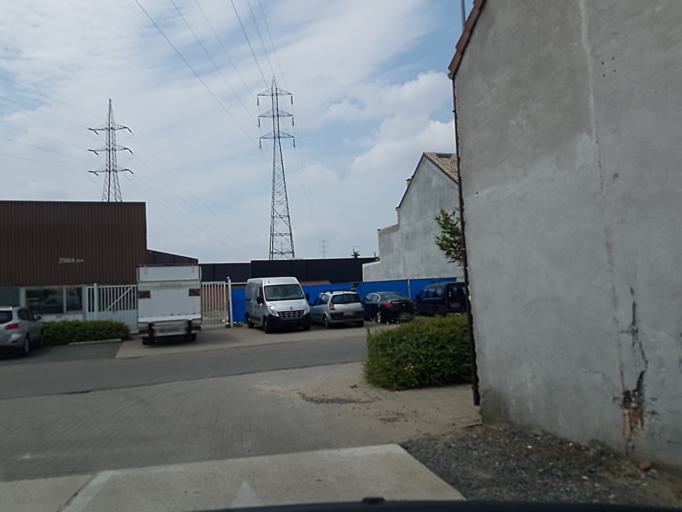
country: BE
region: Flanders
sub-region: Provincie Antwerpen
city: Schoten
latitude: 51.2383
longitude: 4.4766
